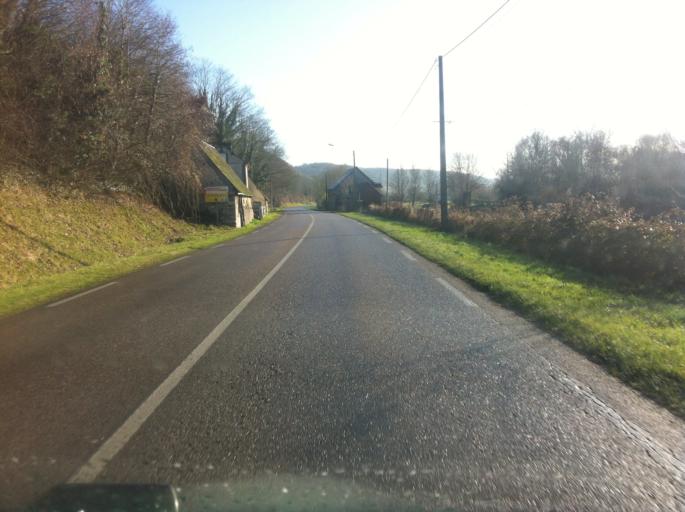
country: FR
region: Haute-Normandie
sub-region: Departement de la Seine-Maritime
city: Saint-Pierre-de-Varengeville
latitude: 49.4839
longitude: 0.9258
